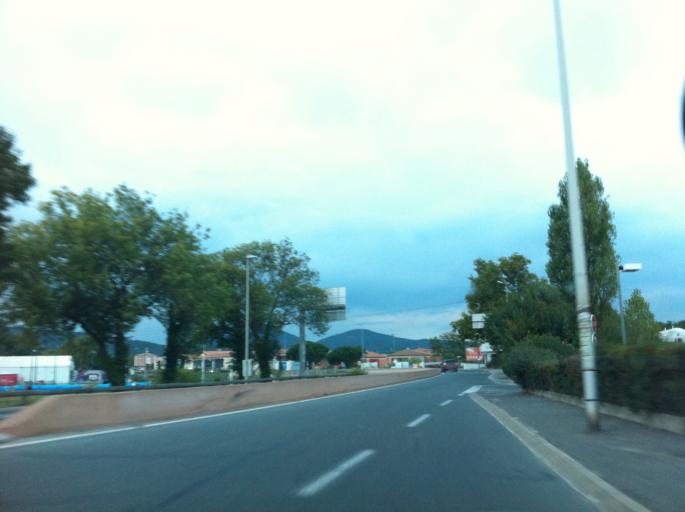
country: FR
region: Provence-Alpes-Cote d'Azur
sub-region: Departement du Var
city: Gassin
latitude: 43.2639
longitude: 6.5768
